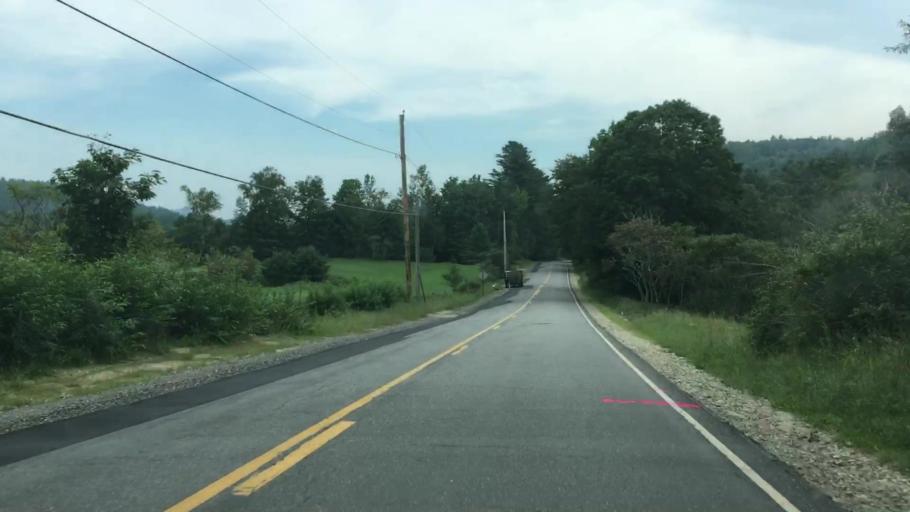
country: US
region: Maine
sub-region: Oxford County
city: Rumford
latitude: 44.5321
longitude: -70.6830
